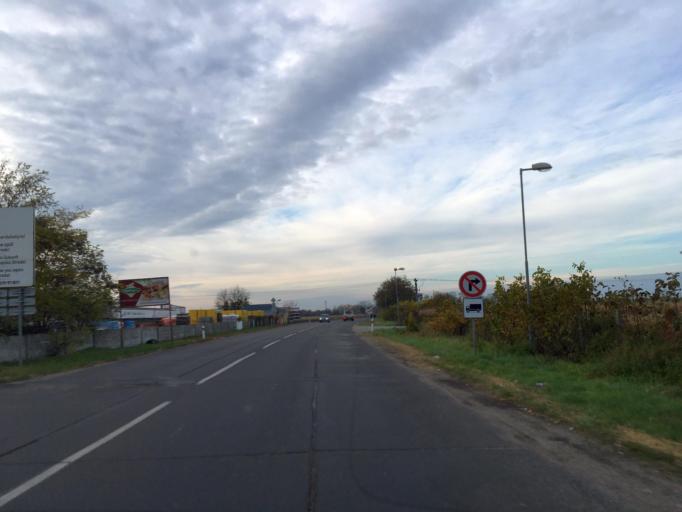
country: SK
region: Trnavsky
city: Dunajska Streda
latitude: 48.0043
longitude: 17.5957
